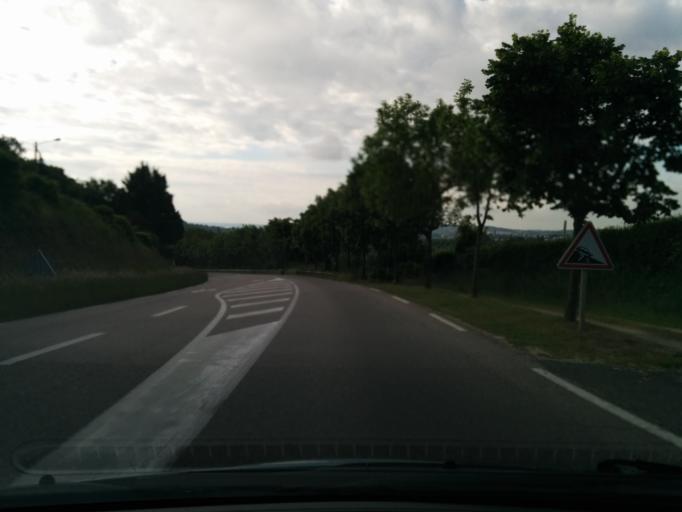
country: FR
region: Ile-de-France
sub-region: Departement des Yvelines
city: Follainville-Dennemont
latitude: 49.0125
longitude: 1.6998
